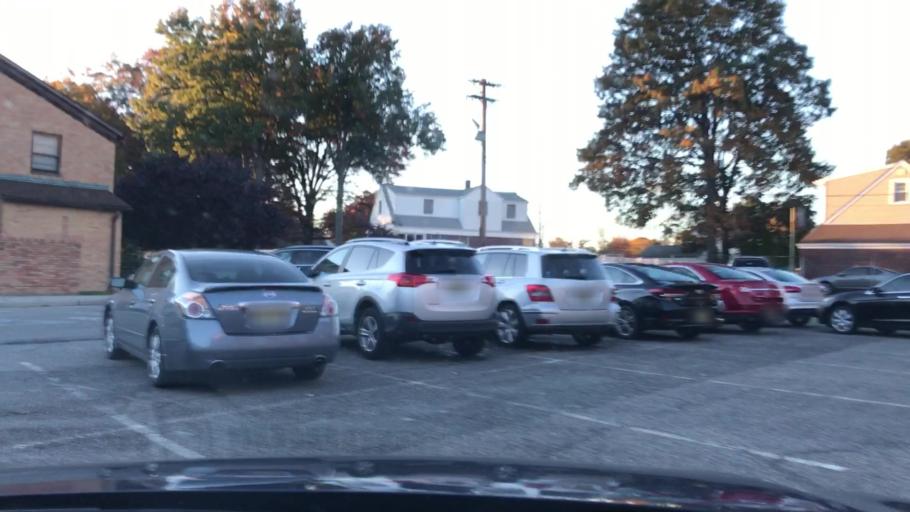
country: US
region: New Jersey
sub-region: Bergen County
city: New Milford
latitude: 40.9179
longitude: -74.0217
